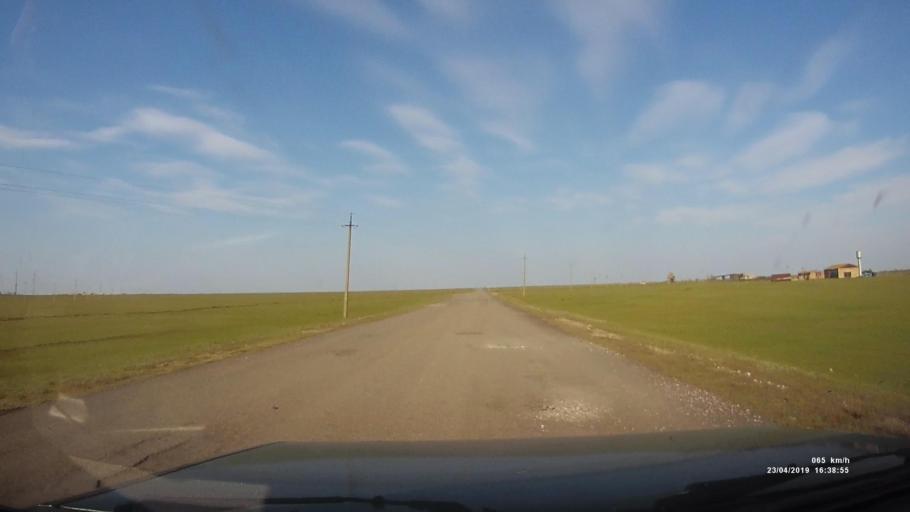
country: RU
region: Kalmykiya
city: Priyutnoye
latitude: 46.3376
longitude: 43.1595
